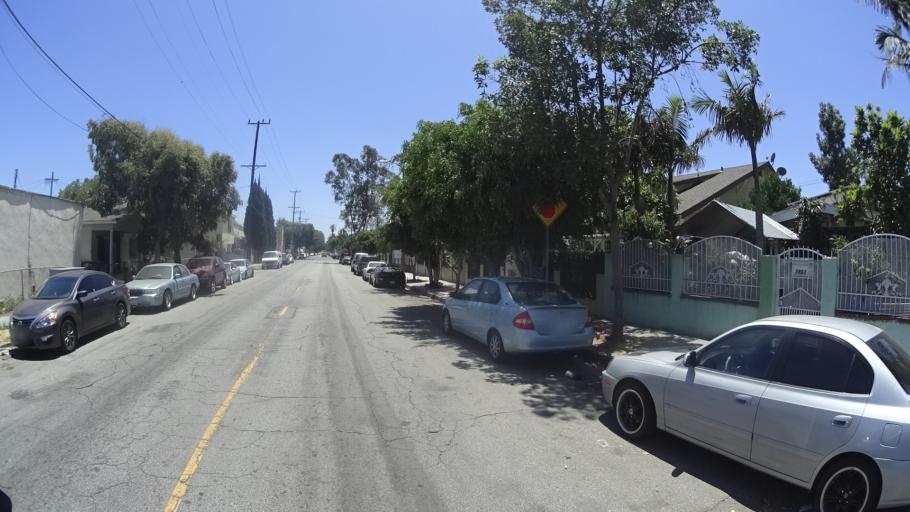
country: US
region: California
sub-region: Los Angeles County
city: View Park-Windsor Hills
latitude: 34.0173
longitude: -118.3045
